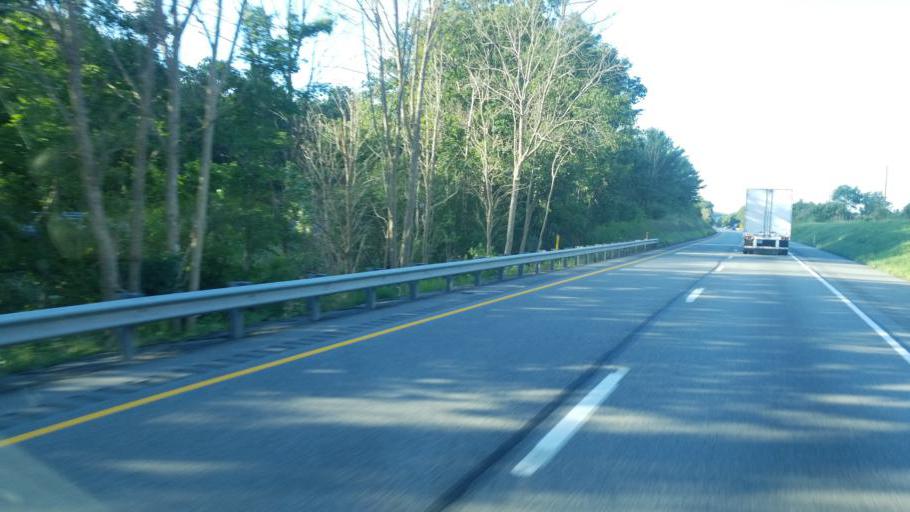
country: US
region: Pennsylvania
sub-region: Bedford County
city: Earlston
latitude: 39.9274
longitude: -78.2335
